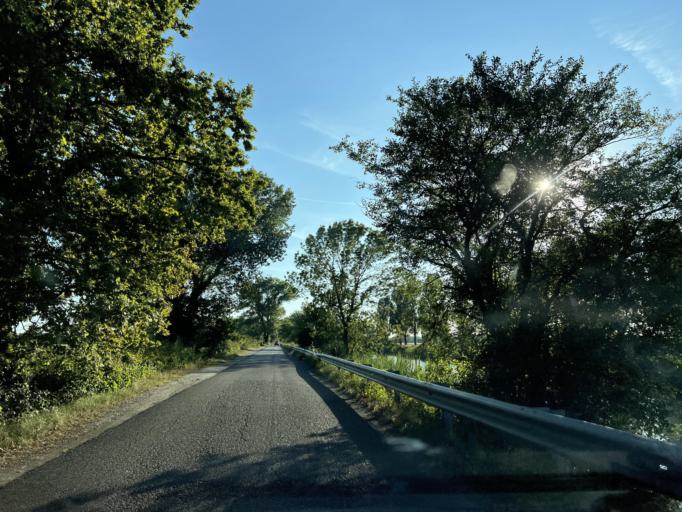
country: IT
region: Friuli Venezia Giulia
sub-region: Provincia di Gorizia
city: Staranzano
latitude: 45.7775
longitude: 13.5047
